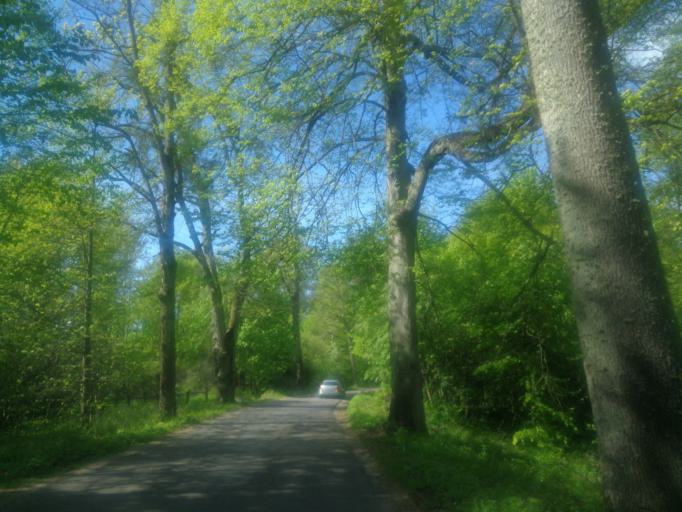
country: PL
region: Warmian-Masurian Voivodeship
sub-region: Powiat ilawski
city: Zalewo
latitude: 53.7504
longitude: 19.6931
